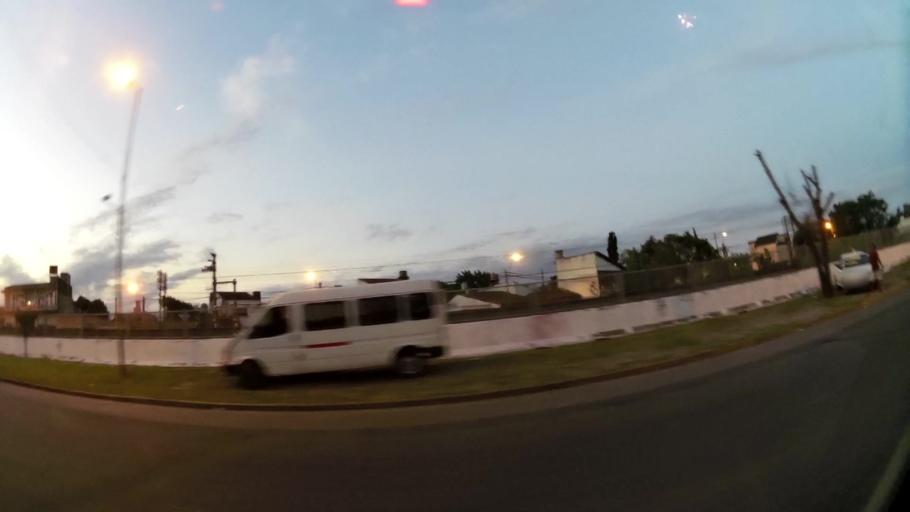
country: AR
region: Buenos Aires
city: Ituzaingo
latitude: -34.6635
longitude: -58.6807
